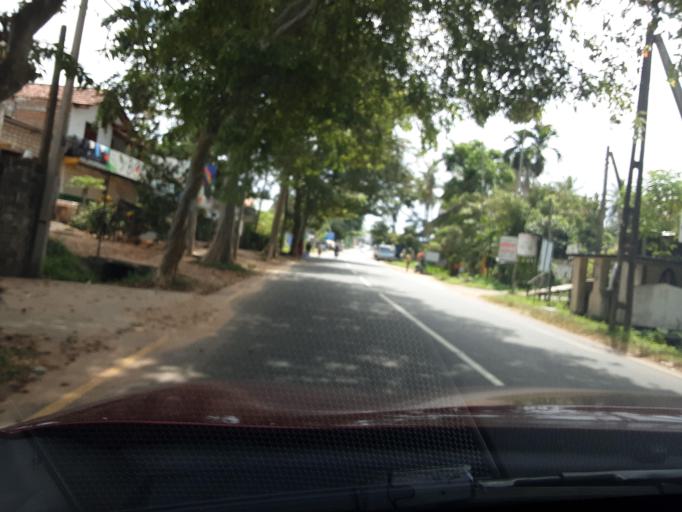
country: LK
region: North Western
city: Kuliyapitiya
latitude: 7.4510
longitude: 80.1881
